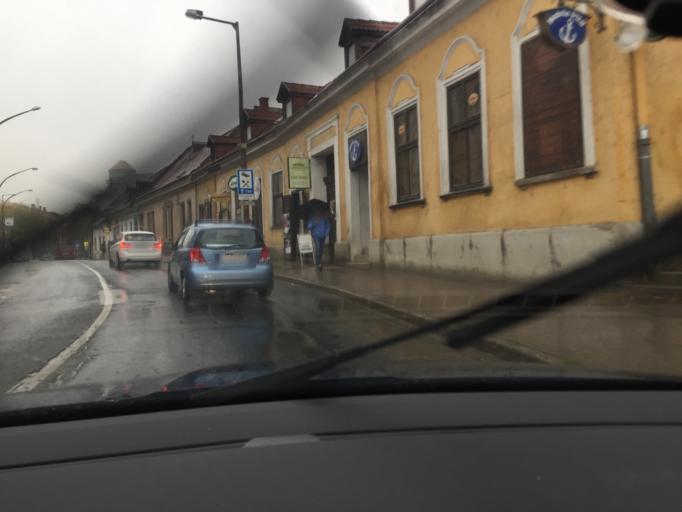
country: HU
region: Komarom-Esztergom
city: Esztergom
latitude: 47.7955
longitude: 18.7416
